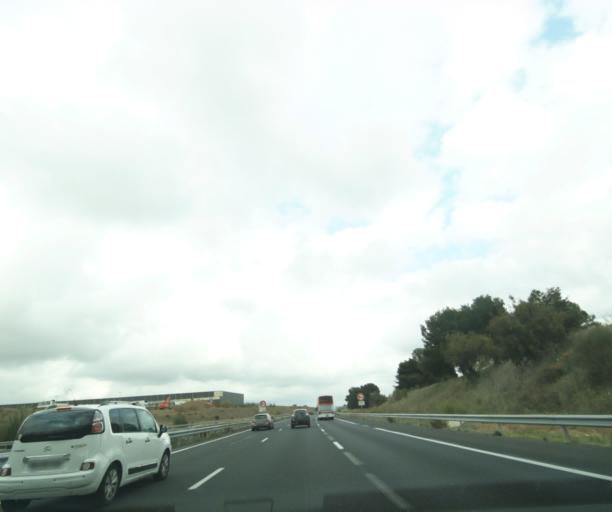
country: FR
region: Languedoc-Roussillon
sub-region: Departement de l'Herault
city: Villeneuve-les-Beziers
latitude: 43.3353
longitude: 3.2868
